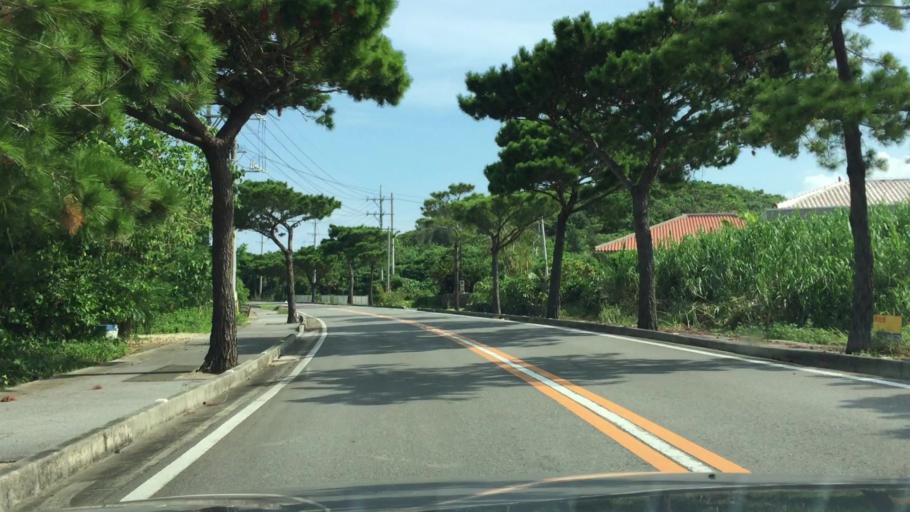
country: JP
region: Okinawa
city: Ishigaki
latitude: 24.4926
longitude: 124.2794
